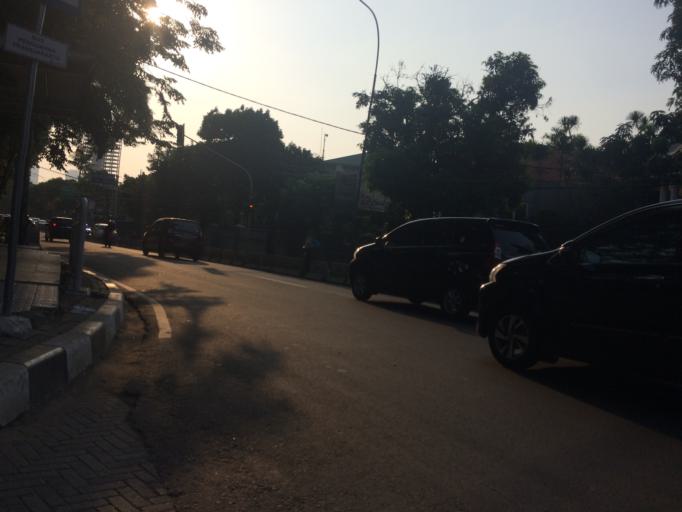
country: ID
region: Jakarta Raya
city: Jakarta
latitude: -6.2026
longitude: 106.8477
